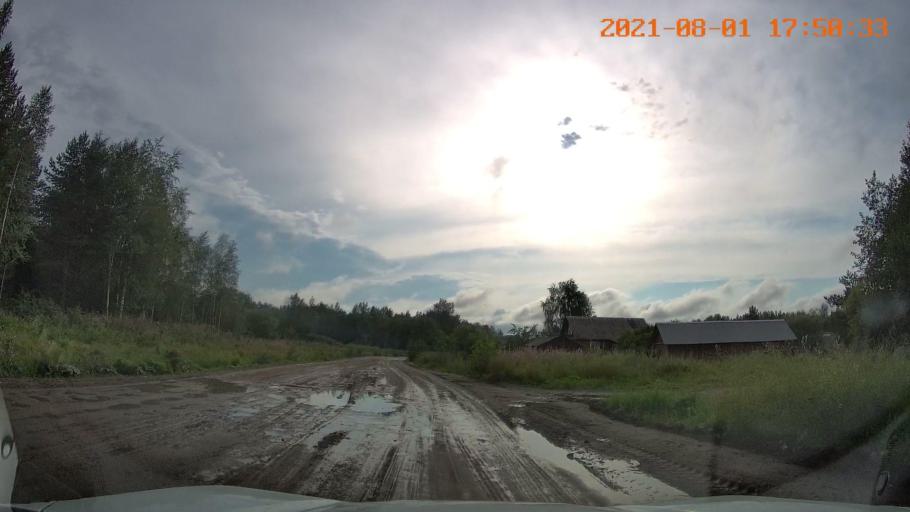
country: RU
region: Leningrad
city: Voznesen'ye
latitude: 60.8556
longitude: 35.8702
